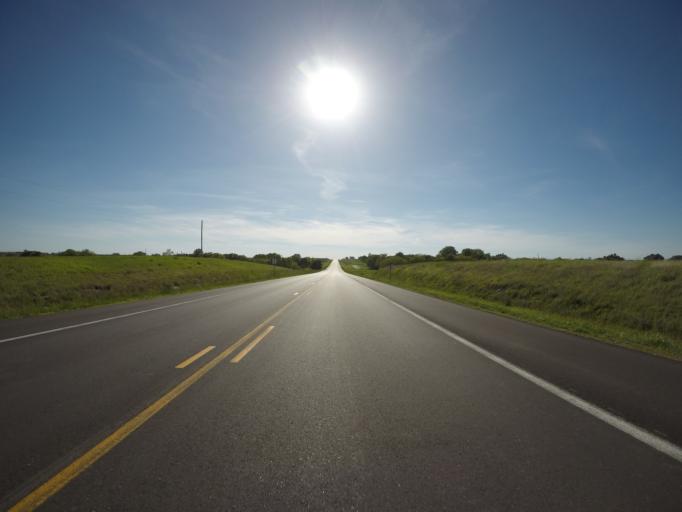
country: US
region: Kansas
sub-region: Clay County
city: Clay Center
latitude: 39.3795
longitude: -96.9856
